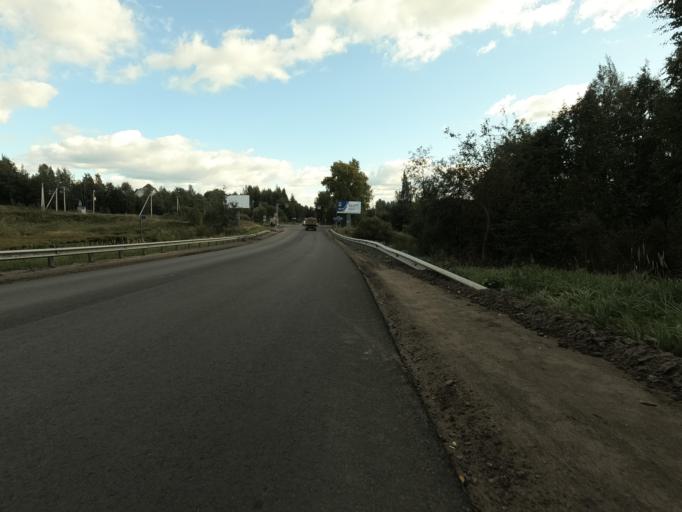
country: RU
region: Leningrad
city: Koltushi
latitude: 59.9710
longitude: 30.6533
